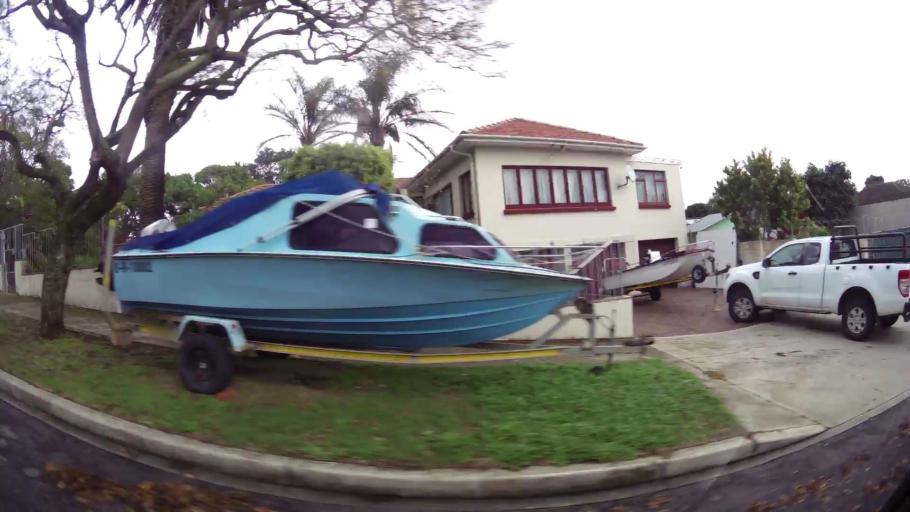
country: ZA
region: Eastern Cape
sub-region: Nelson Mandela Bay Metropolitan Municipality
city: Port Elizabeth
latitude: -33.9531
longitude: 25.5937
